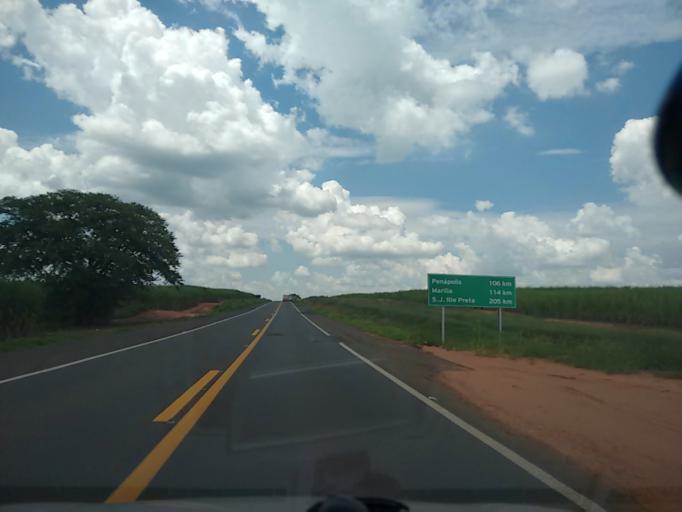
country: BR
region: Sao Paulo
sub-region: Osvaldo Cruz
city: Osvaldo Cruz
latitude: -21.9045
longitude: -50.8856
